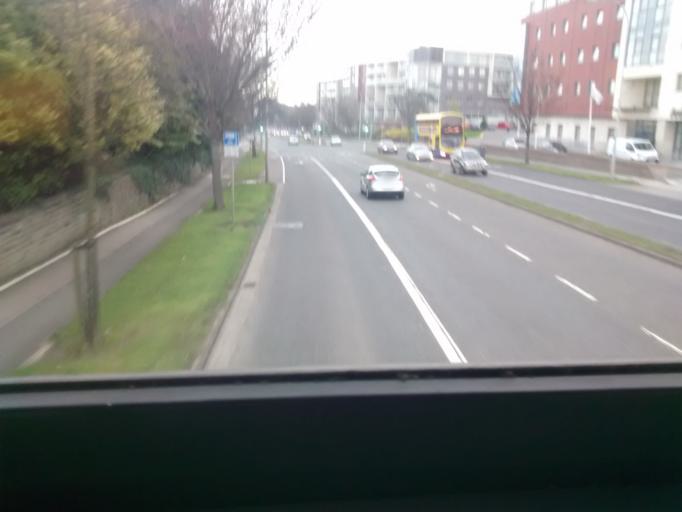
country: IE
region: Leinster
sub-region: Dublin City
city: Finglas
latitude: 53.3827
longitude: -6.2922
